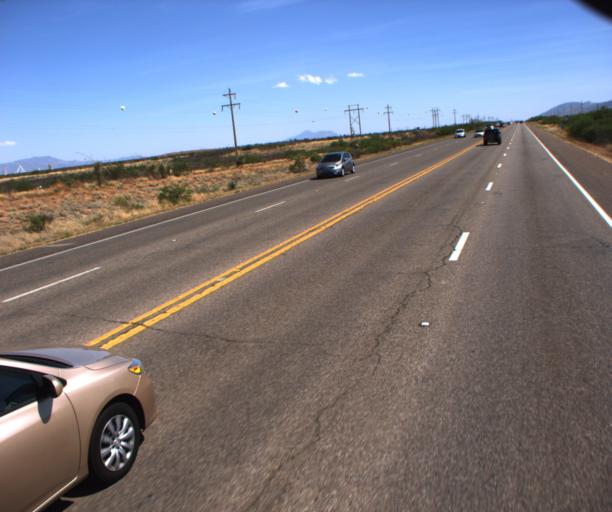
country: US
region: Arizona
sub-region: Cochise County
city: Huachuca City
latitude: 31.5910
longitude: -110.3231
